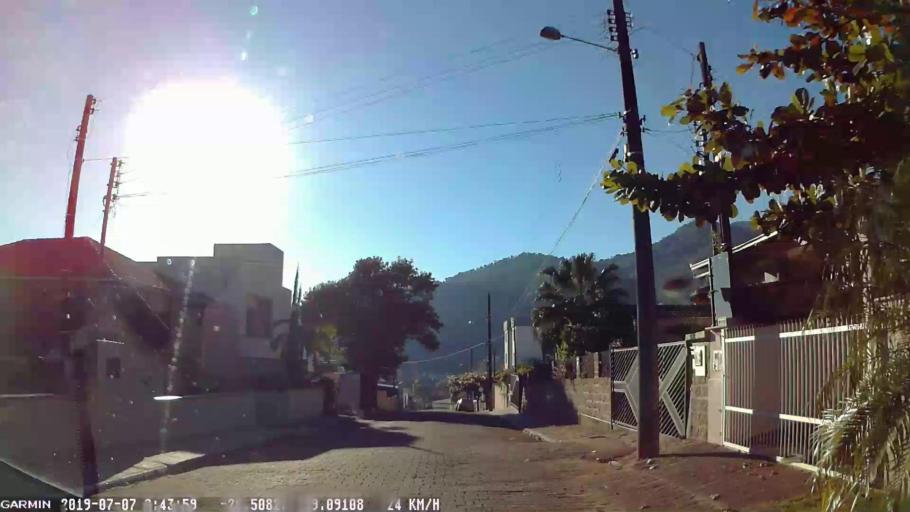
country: BR
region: Santa Catarina
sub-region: Jaragua Do Sul
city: Jaragua do Sul
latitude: -26.5082
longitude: -49.0911
